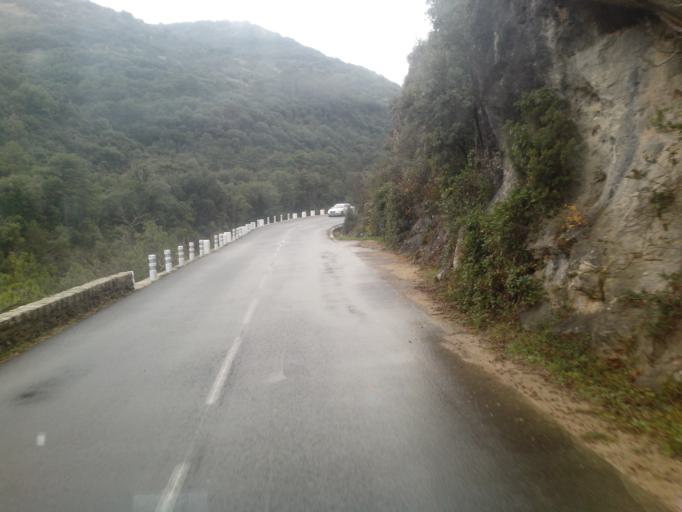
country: FR
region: Languedoc-Roussillon
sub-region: Departement de l'Herault
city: Saint-Jean-de-Fos
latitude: 43.7410
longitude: 3.5591
